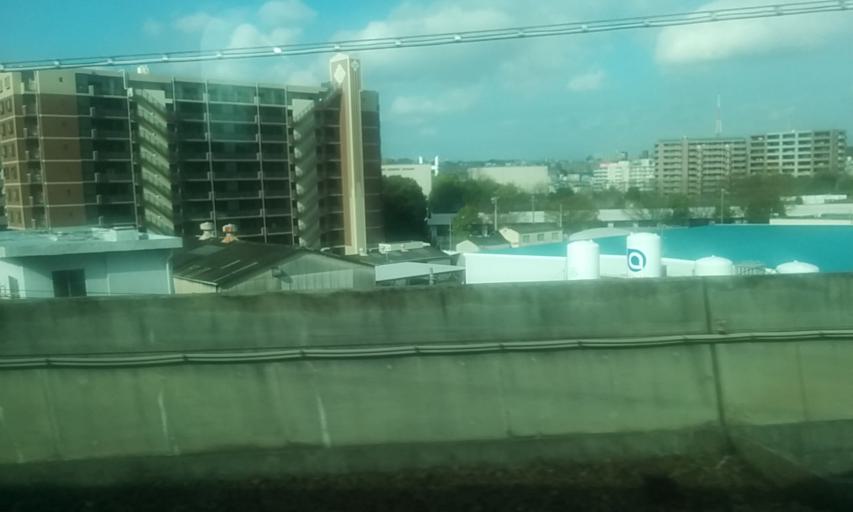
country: JP
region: Kanagawa
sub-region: Kawasaki-shi
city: Kawasaki
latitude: 35.5203
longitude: 139.6814
